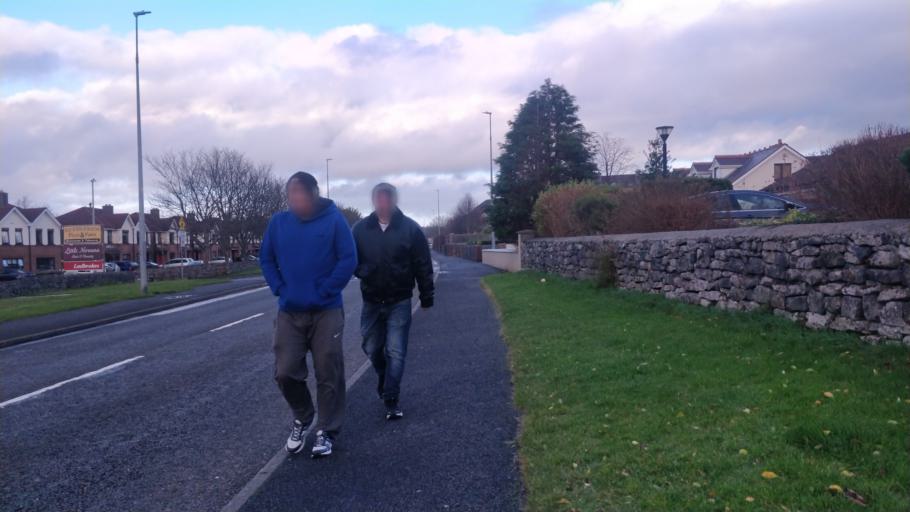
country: IE
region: Connaught
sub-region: County Galway
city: Gaillimh
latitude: 53.2890
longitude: -9.0000
